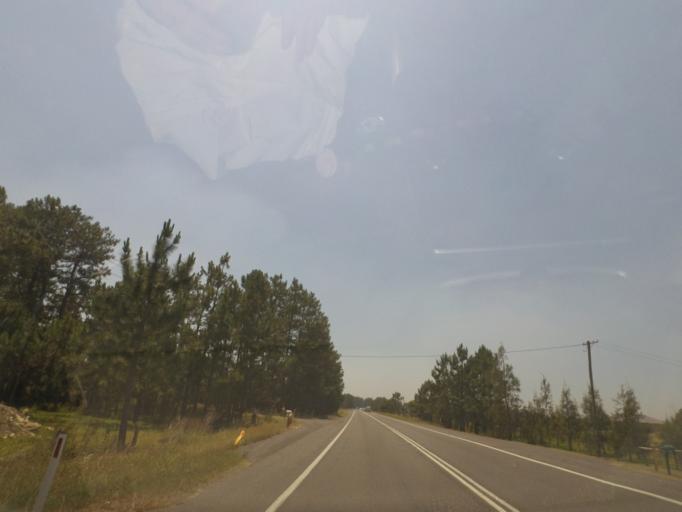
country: AU
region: New South Wales
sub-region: Port Stephens Shire
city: Medowie
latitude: -32.8065
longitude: 151.8757
